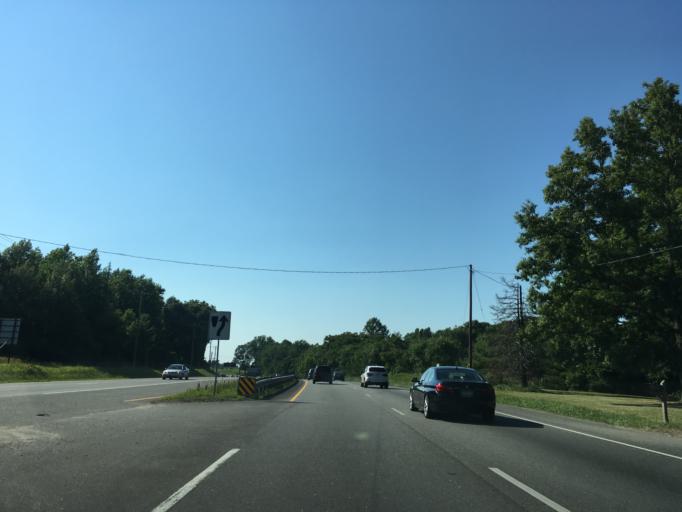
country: US
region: Maryland
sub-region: Queen Anne's County
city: Centreville
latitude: 38.9472
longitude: -76.0644
